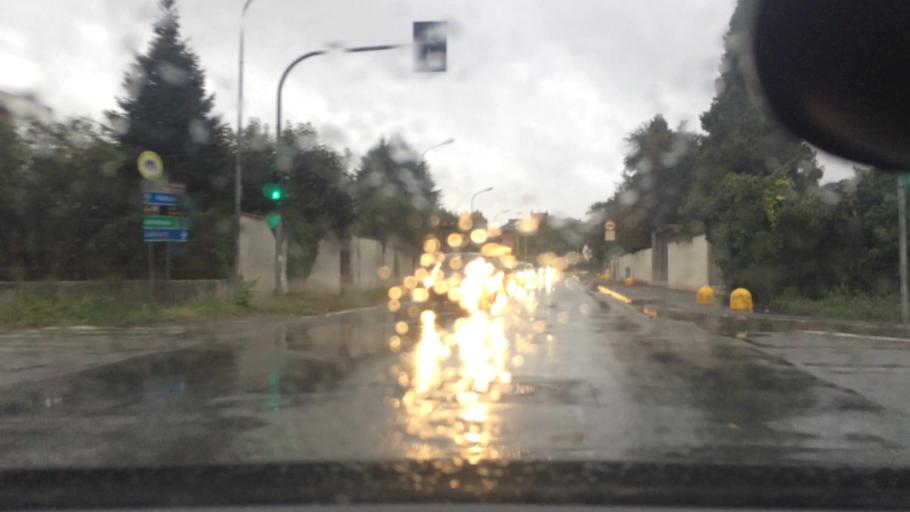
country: IT
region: Lombardy
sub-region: Citta metropolitana di Milano
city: Nerviano
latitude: 45.5463
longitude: 8.9754
